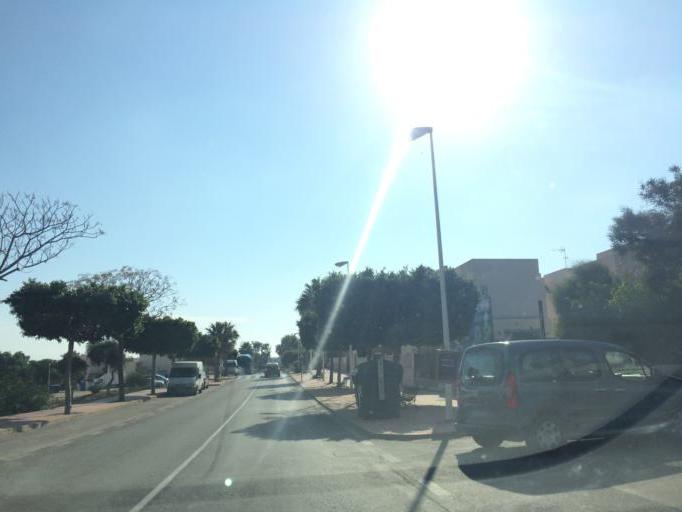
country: ES
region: Andalusia
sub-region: Provincia de Almeria
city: San Jose
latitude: 36.7647
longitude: -2.1105
